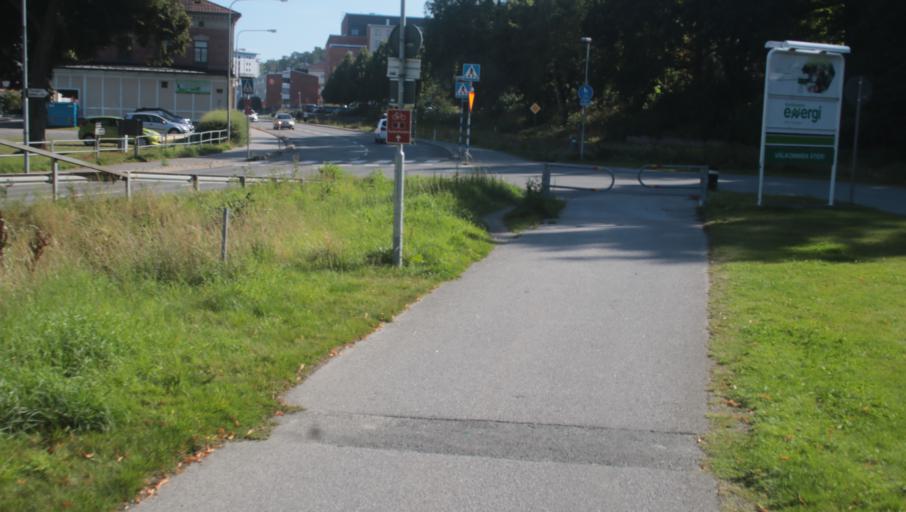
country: SE
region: Blekinge
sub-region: Karlshamns Kommun
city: Karlshamn
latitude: 56.1757
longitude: 14.8549
